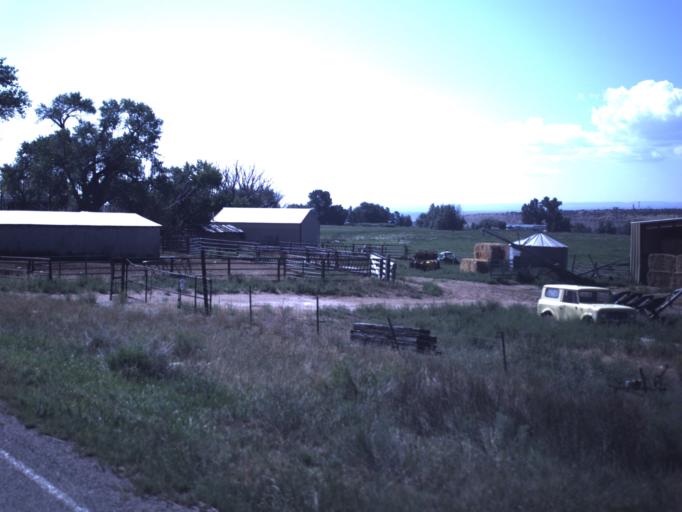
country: US
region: Utah
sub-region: Duchesne County
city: Duchesne
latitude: 40.2634
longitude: -110.4135
